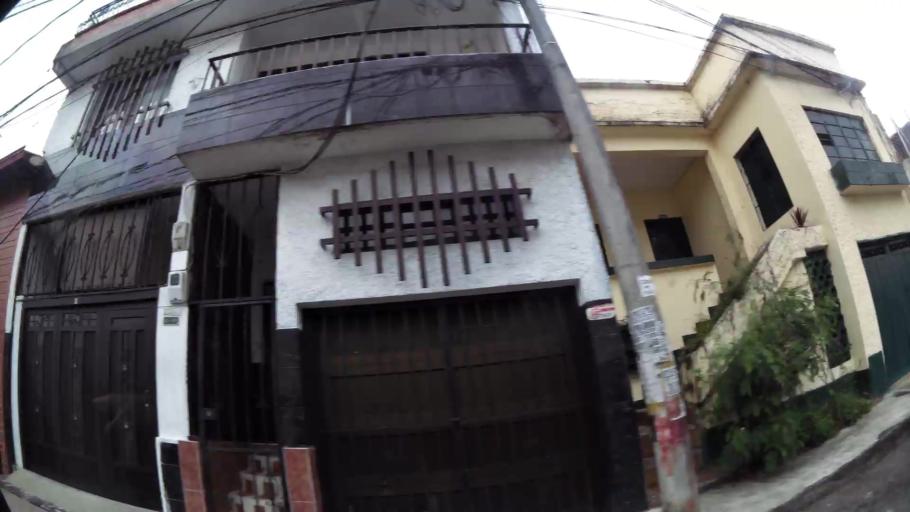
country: CO
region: Antioquia
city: Medellin
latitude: 6.2754
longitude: -75.5944
